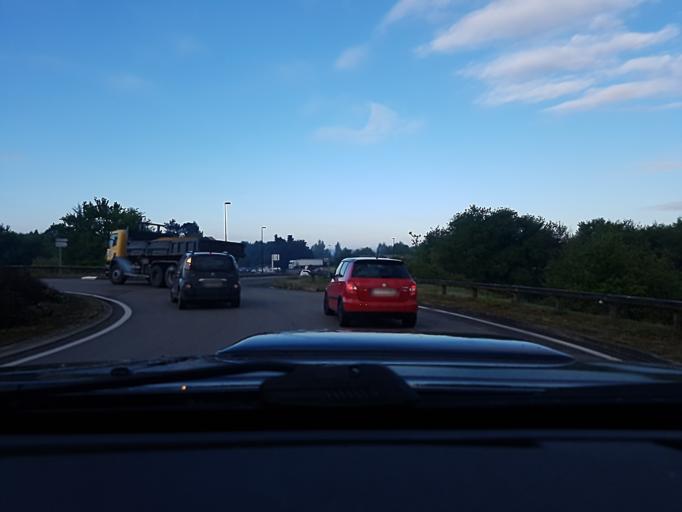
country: FR
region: Pays de la Loire
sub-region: Departement de la Vendee
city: Aizenay
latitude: 46.7471
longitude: -1.6244
